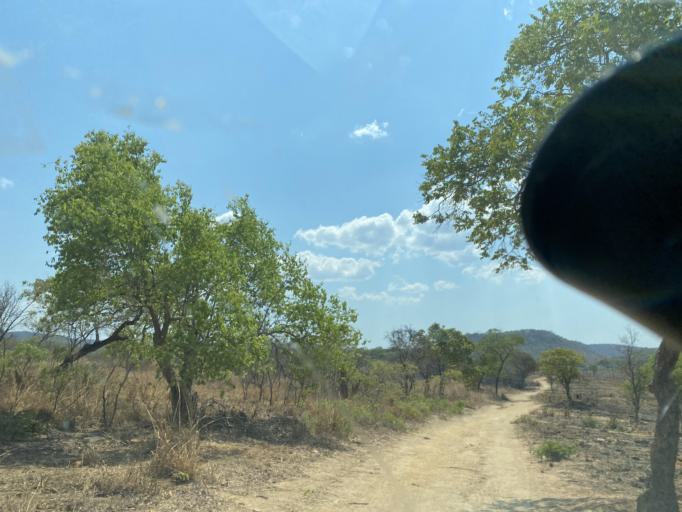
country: ZM
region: Lusaka
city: Chongwe
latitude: -15.0847
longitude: 29.4817
